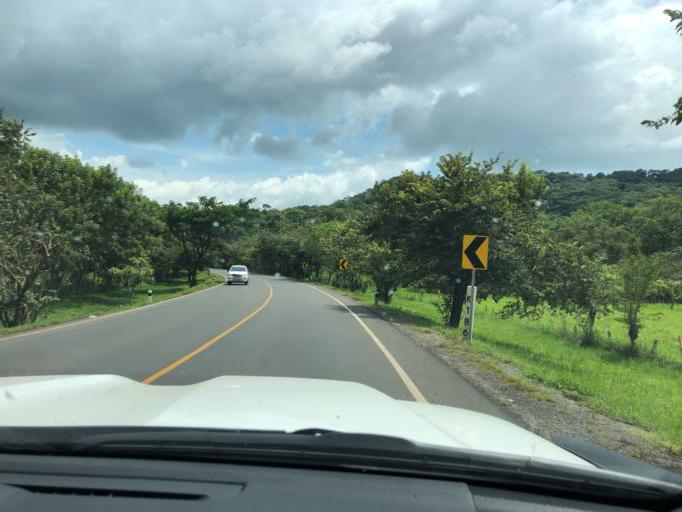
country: NI
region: Chontales
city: Villa Sandino
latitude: 12.0560
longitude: -85.0389
